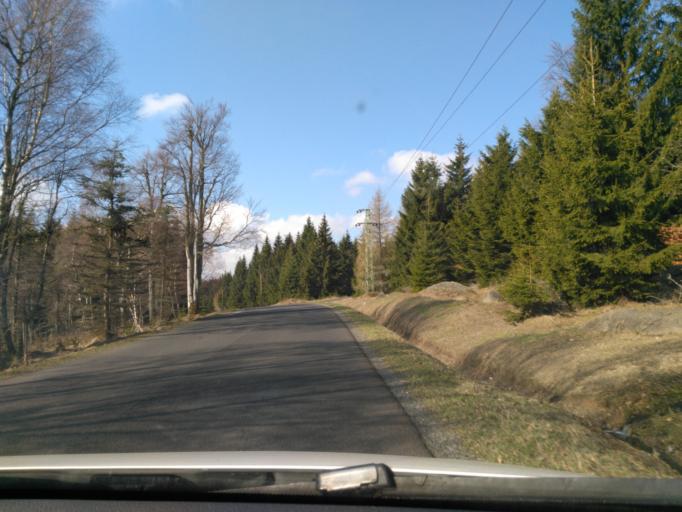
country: CZ
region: Ustecky
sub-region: Okres Chomutov
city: Kovarska
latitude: 50.4563
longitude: 13.0846
